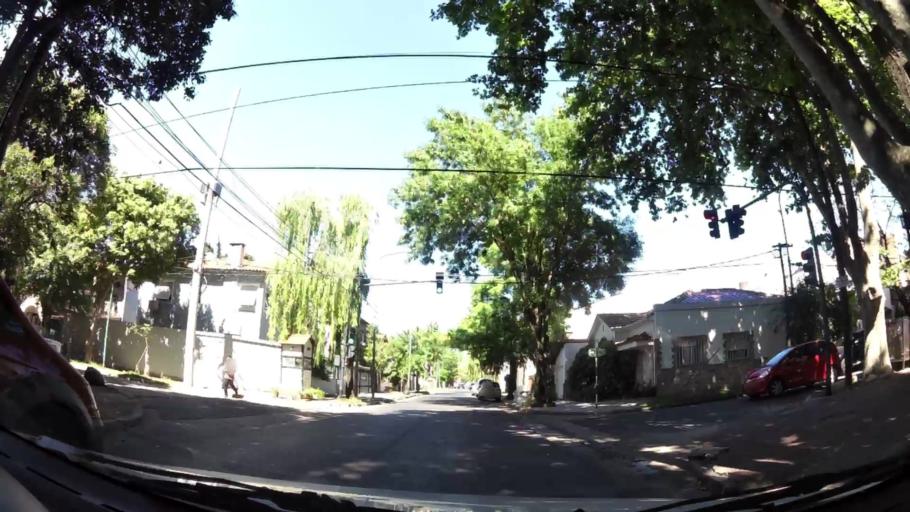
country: AR
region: Buenos Aires
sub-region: Partido de Vicente Lopez
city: Olivos
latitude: -34.5186
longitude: -58.4936
